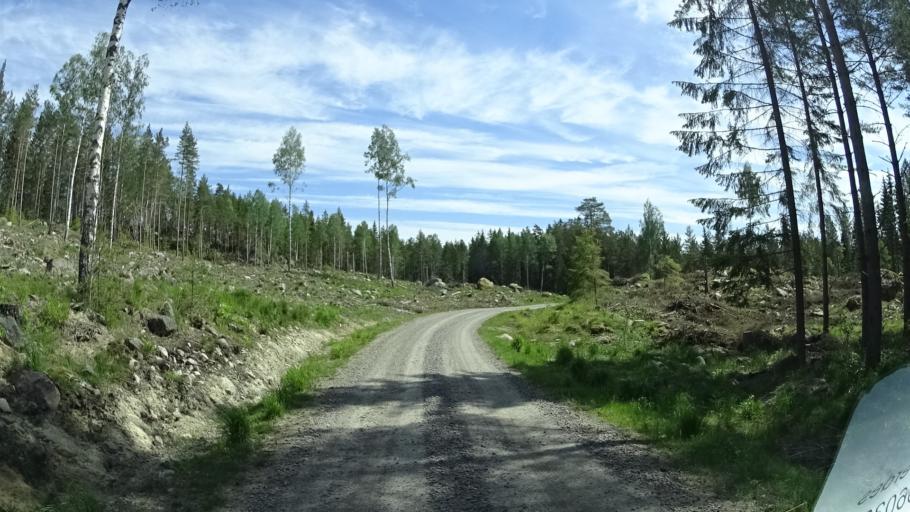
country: SE
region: OEstergoetland
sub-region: Norrkopings Kommun
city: Svartinge
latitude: 58.7802
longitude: 15.9255
